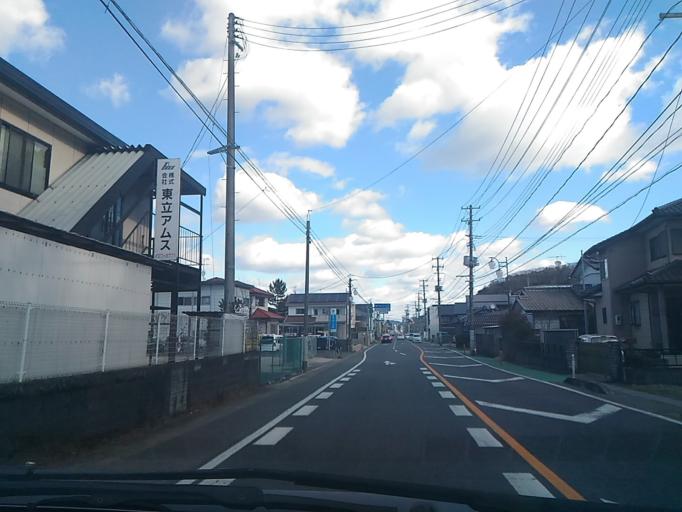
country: JP
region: Fukushima
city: Iwaki
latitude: 37.0306
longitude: 140.8504
